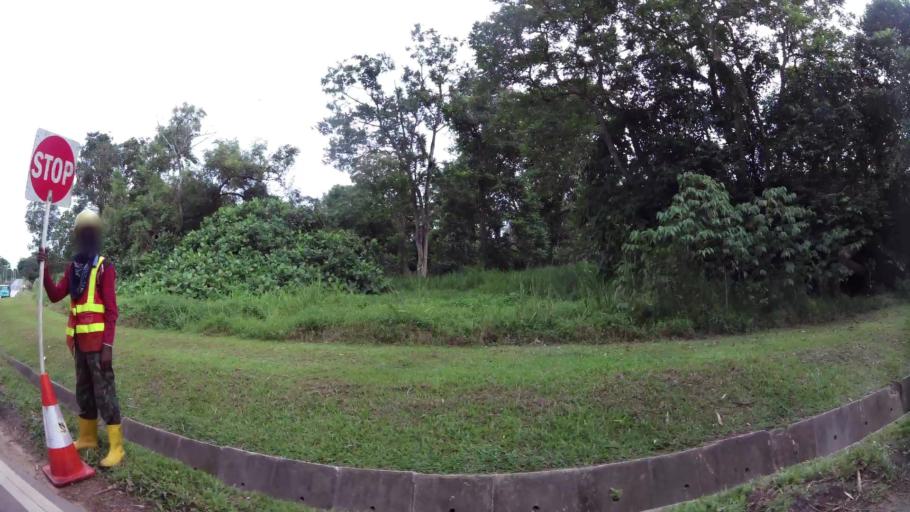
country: MY
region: Johor
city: Johor Bahru
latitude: 1.4221
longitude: 103.7176
